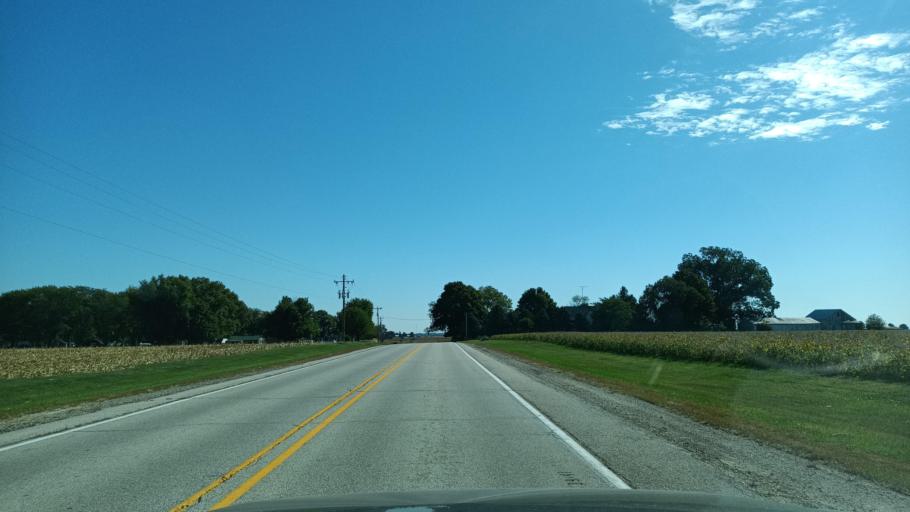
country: US
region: Illinois
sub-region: Knox County
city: Knoxville
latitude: 40.9078
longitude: -90.2388
